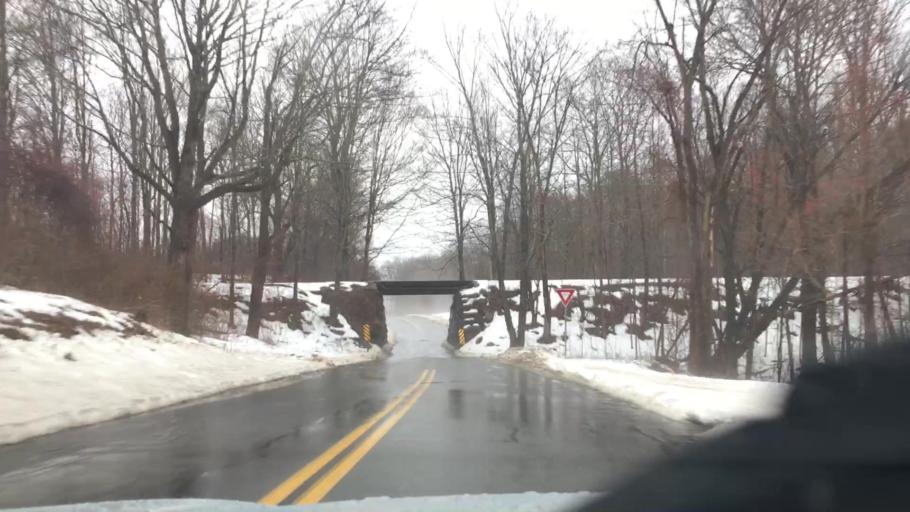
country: US
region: Massachusetts
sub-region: Hampshire County
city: Belchertown
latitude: 42.2853
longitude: -72.4215
